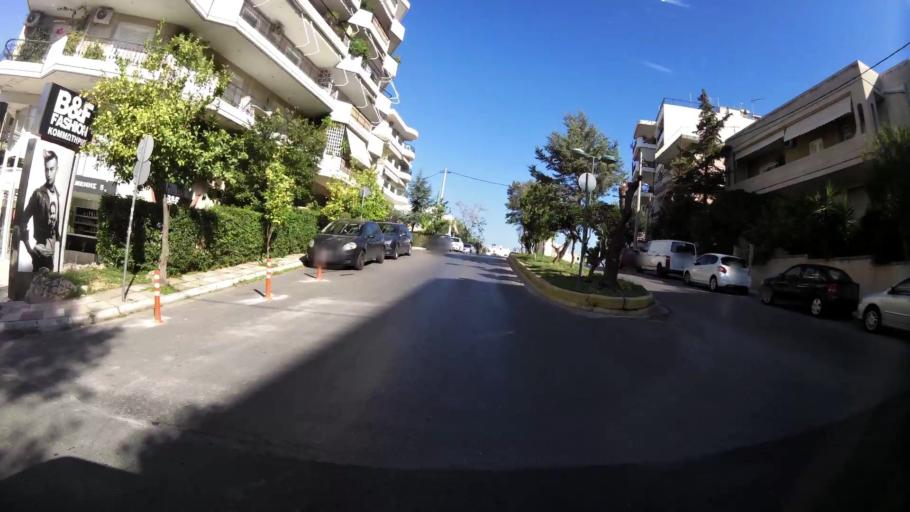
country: GR
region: Attica
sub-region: Nomarchia Athinas
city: Metamorfosi
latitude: 38.0635
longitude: 23.7645
